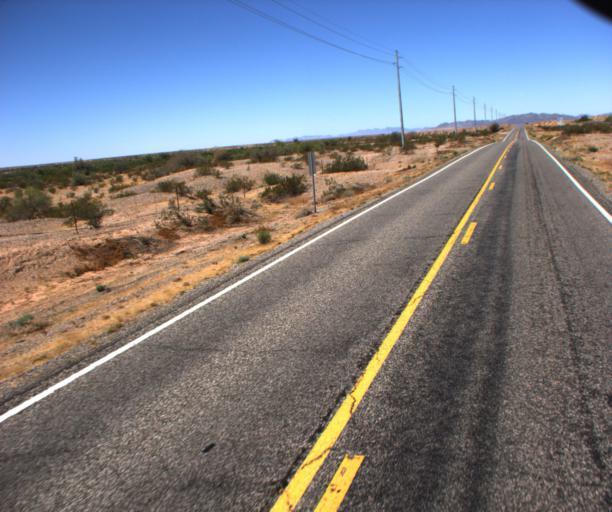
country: US
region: Arizona
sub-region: La Paz County
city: Cienega Springs
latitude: 33.9940
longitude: -114.0976
